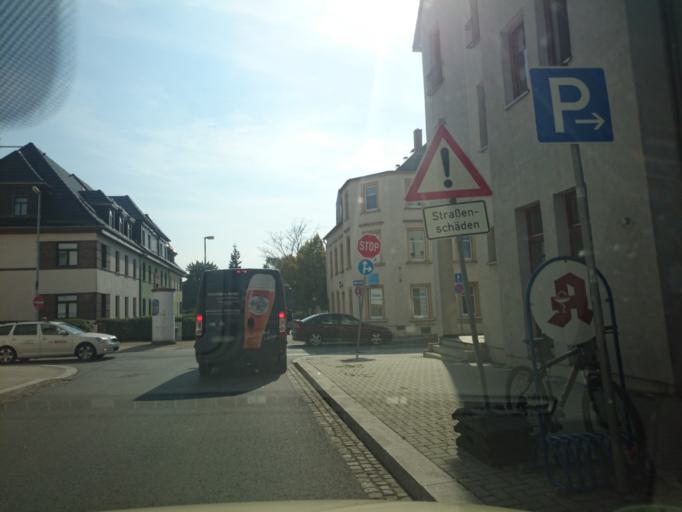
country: DE
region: Saxony
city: Brand-Erbisdorf
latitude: 50.8714
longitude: 13.3242
